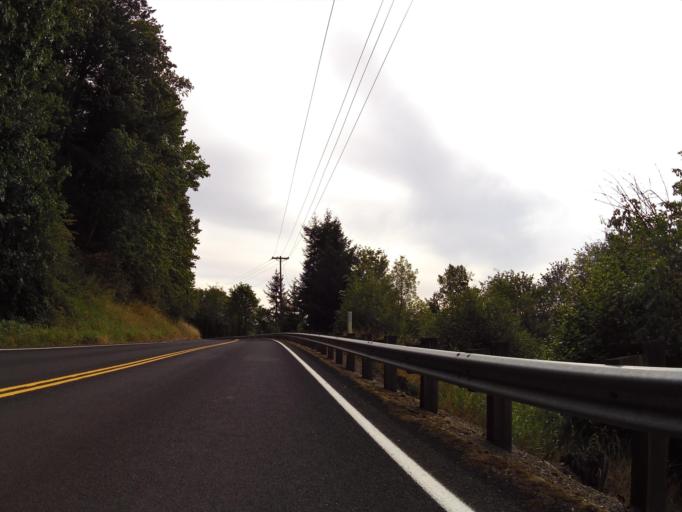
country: US
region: Washington
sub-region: Cowlitz County
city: Castle Rock
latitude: 46.2465
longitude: -122.8879
